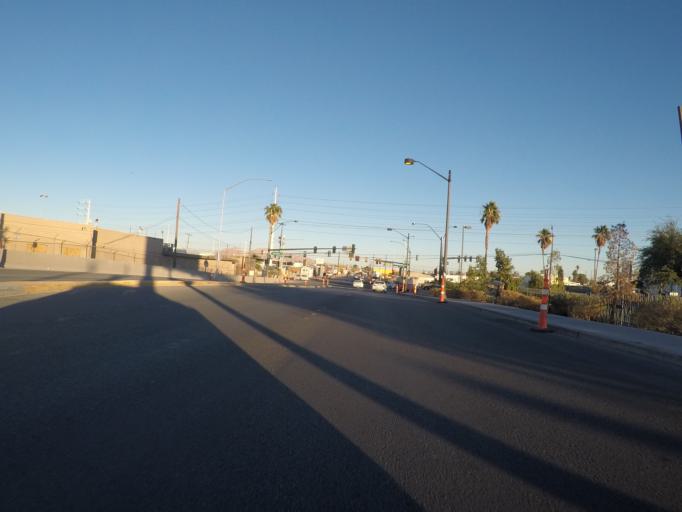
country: US
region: Nevada
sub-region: Clark County
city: Las Vegas
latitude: 36.1524
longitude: -115.1603
